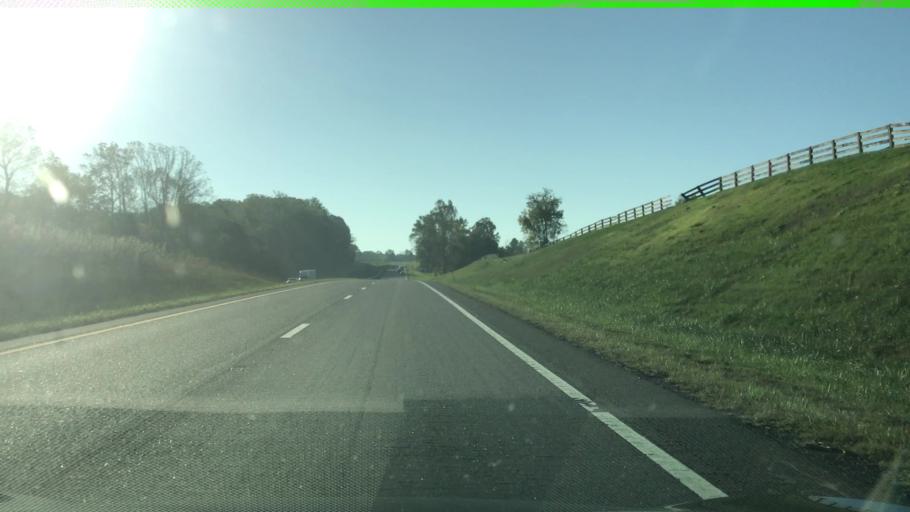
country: US
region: Virginia
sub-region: Bedford County
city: Forest
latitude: 37.3068
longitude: -79.3914
